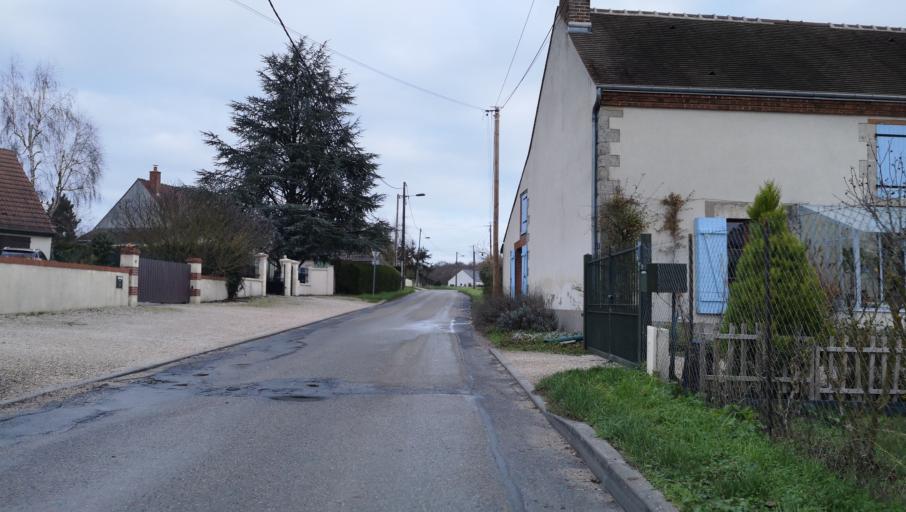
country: FR
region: Centre
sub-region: Departement du Loiret
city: Boigny-sur-Bionne
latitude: 47.9115
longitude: 2.0030
